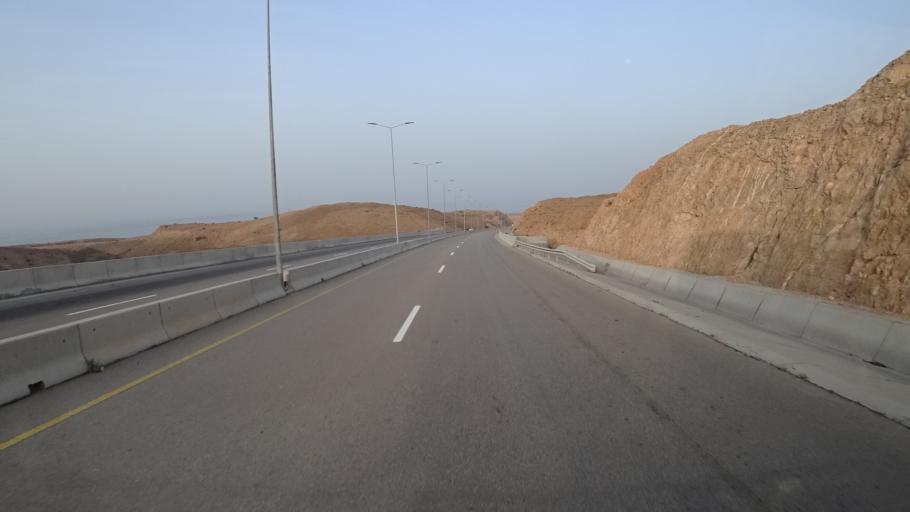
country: OM
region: Ash Sharqiyah
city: Al Qabil
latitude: 23.0930
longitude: 59.0136
